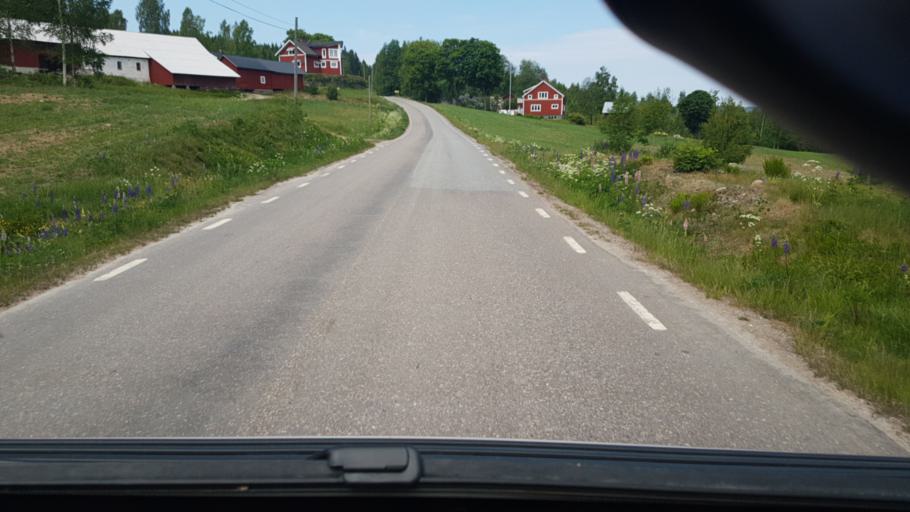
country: SE
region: Vaermland
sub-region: Arvika Kommun
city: Arvika
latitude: 59.7827
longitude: 12.7694
